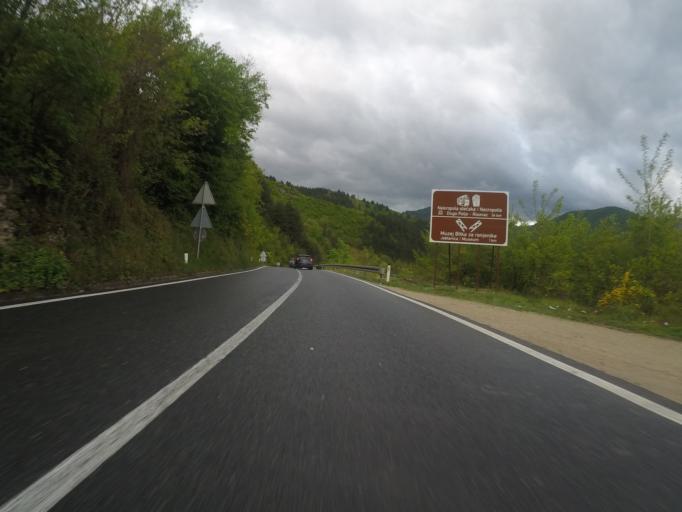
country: BA
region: Federation of Bosnia and Herzegovina
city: Jablanica
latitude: 43.6484
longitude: 17.7552
